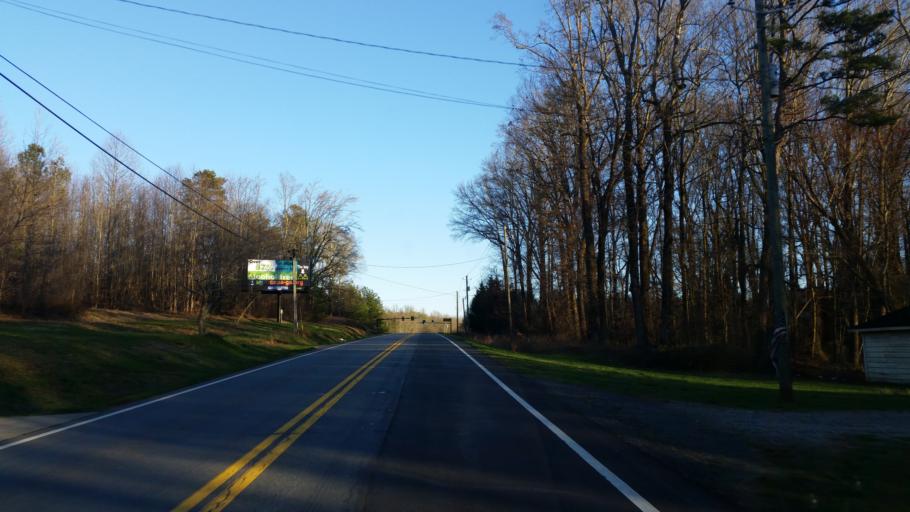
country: US
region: Georgia
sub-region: Dawson County
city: Dawsonville
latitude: 34.4127
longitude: -84.1085
